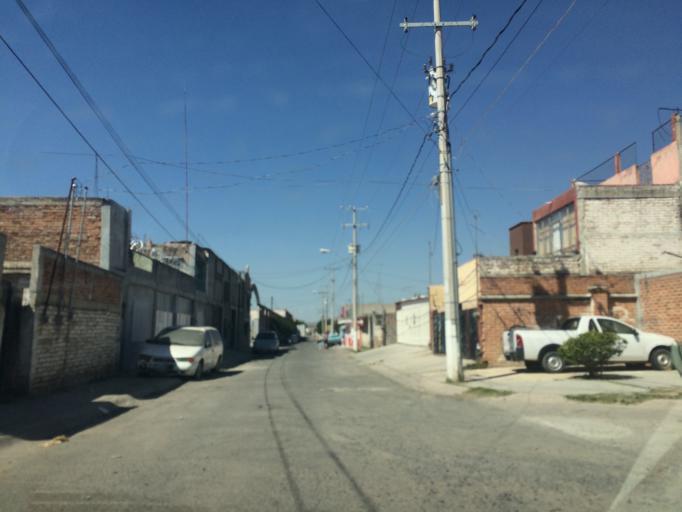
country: MX
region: Guanajuato
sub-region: Leon
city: San Jose de Duran (Los Troncoso)
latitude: 21.0887
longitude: -101.6621
